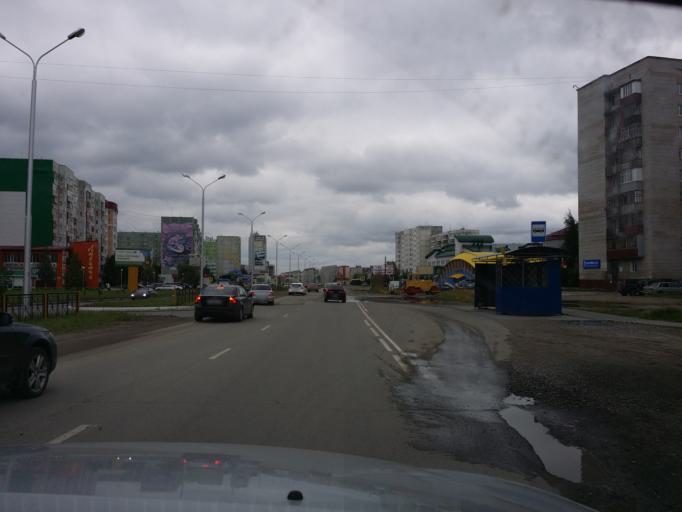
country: RU
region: Khanty-Mansiyskiy Avtonomnyy Okrug
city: Nizhnevartovsk
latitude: 60.9498
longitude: 76.5882
